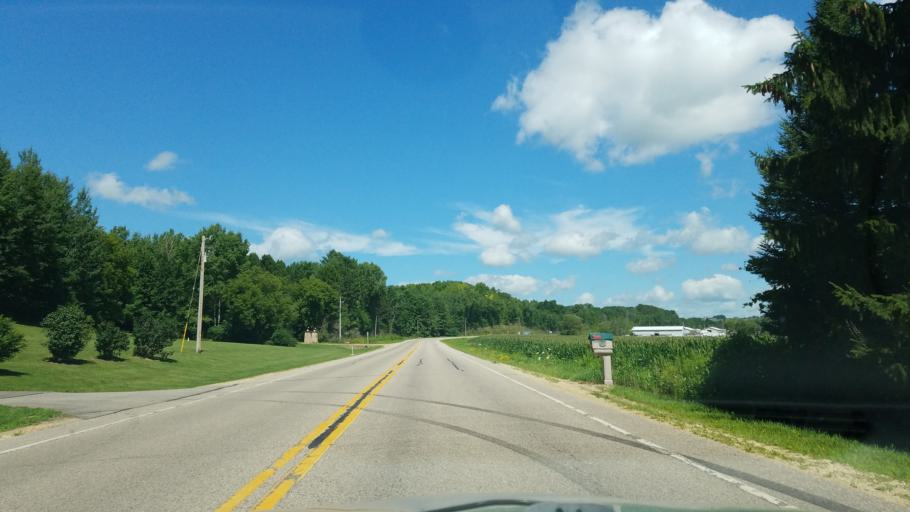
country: US
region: Wisconsin
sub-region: Saint Croix County
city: Glenwood City
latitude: 45.0481
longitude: -92.1753
